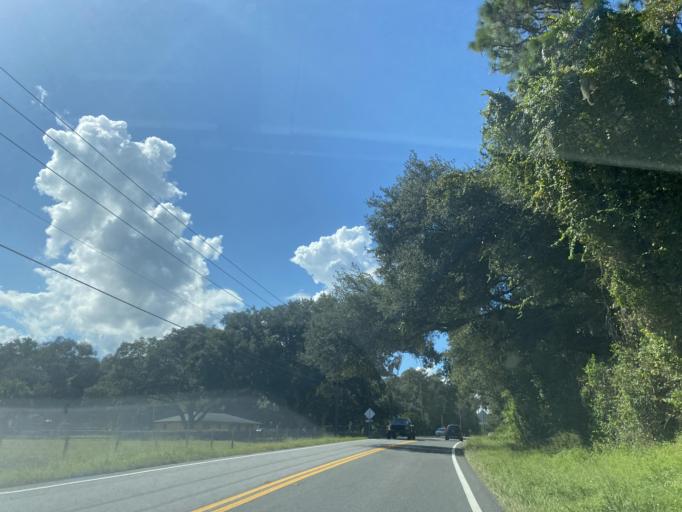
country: US
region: Florida
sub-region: Lake County
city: Lady Lake
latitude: 28.9828
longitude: -81.8968
